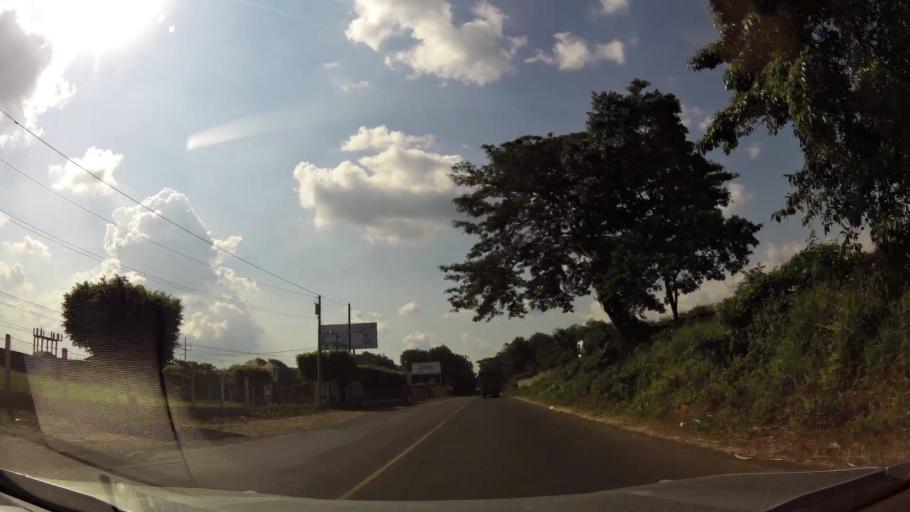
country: GT
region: Retalhuleu
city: San Sebastian
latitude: 14.5505
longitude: -91.6292
